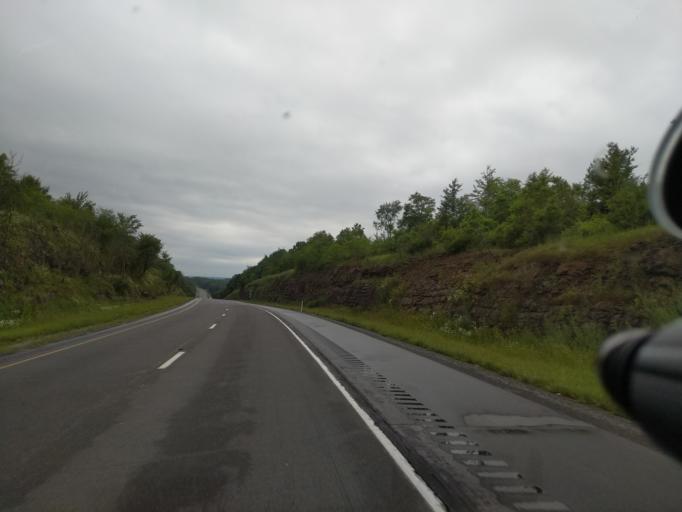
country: US
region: Pennsylvania
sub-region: Lycoming County
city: Jersey Shore
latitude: 41.0653
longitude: -77.2181
